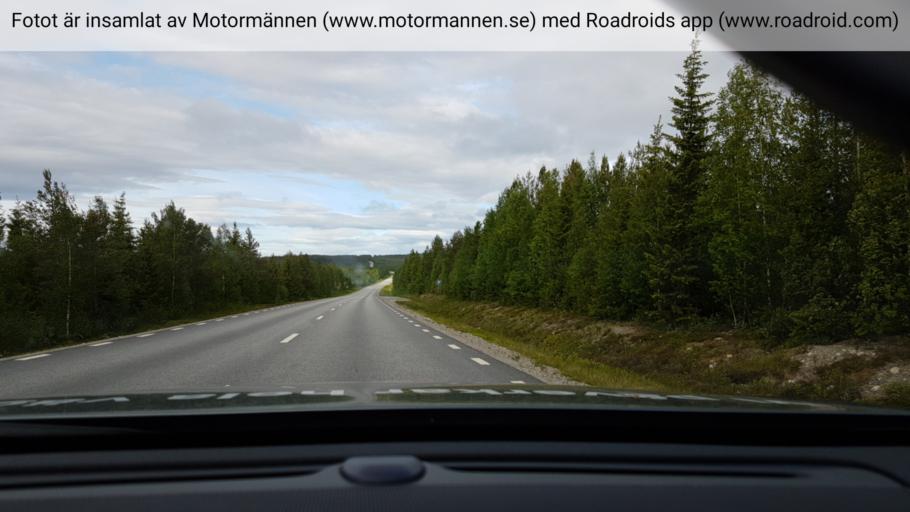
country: SE
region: Vaesterbotten
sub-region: Asele Kommun
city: Insjon
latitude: 64.1968
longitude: 17.5773
